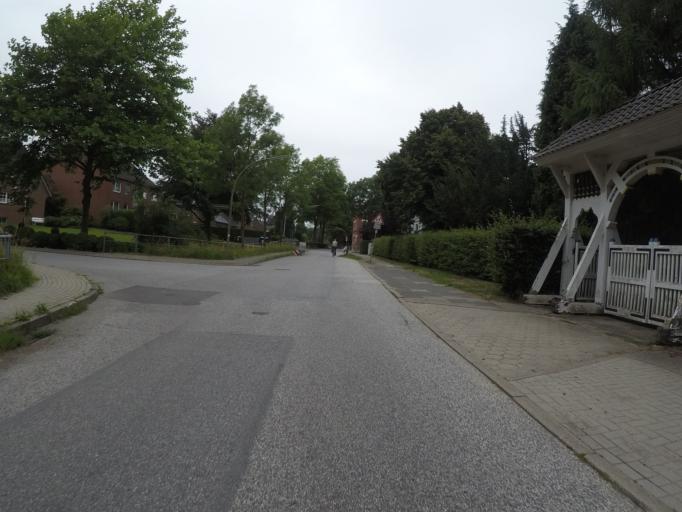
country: DE
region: Hamburg
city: Altona
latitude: 53.5275
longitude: 9.8655
